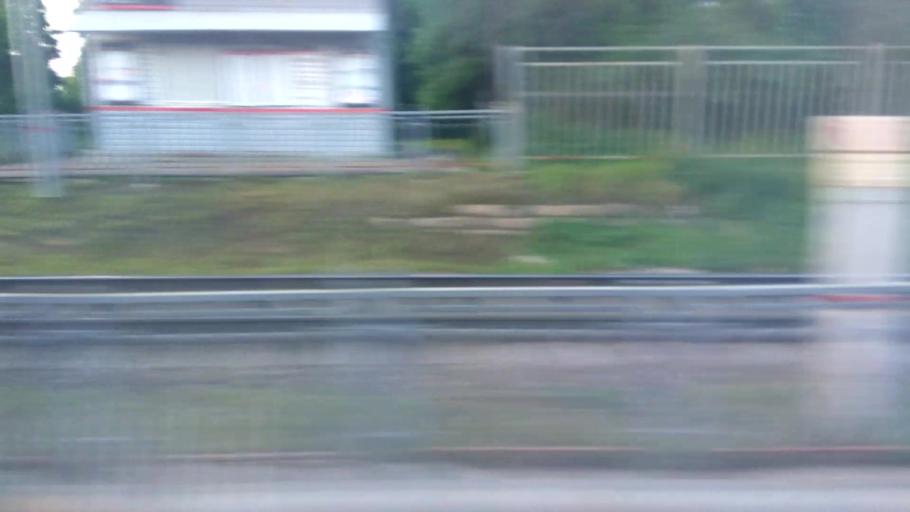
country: RU
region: Moskovskaya
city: Vostryakovo
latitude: 55.3836
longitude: 37.8138
